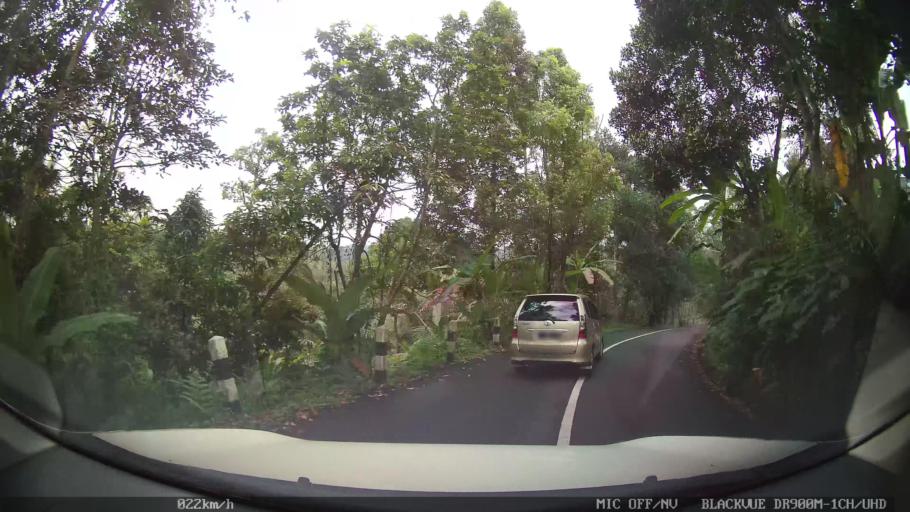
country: ID
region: Bali
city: Peneng
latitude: -8.3638
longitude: 115.1841
